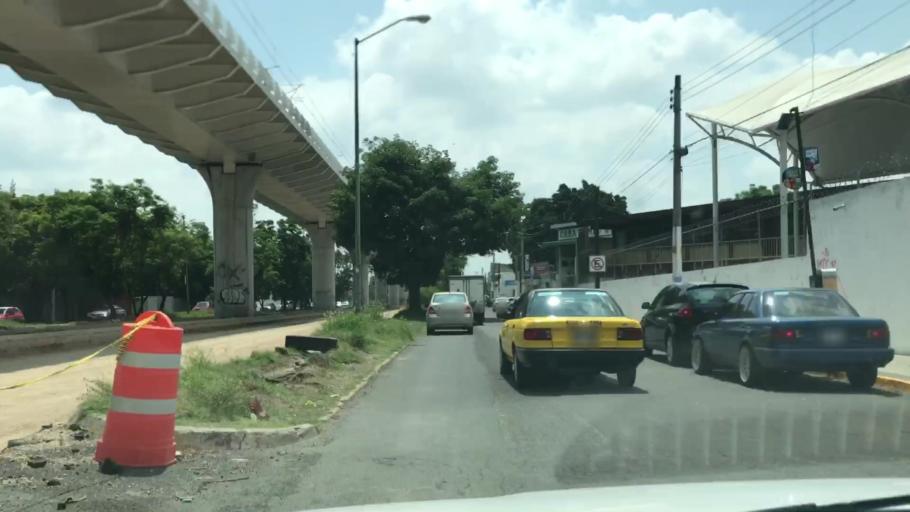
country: MX
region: Jalisco
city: Zapopan2
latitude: 20.7358
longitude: -103.4001
